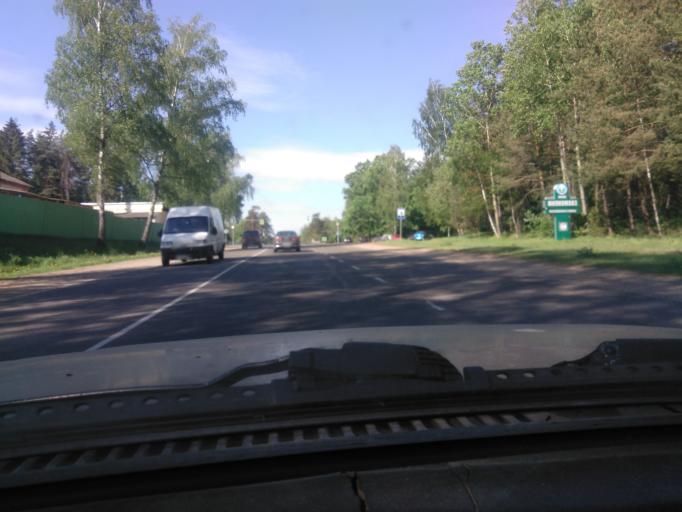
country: BY
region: Mogilev
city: Buynichy
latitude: 53.8116
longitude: 30.2277
